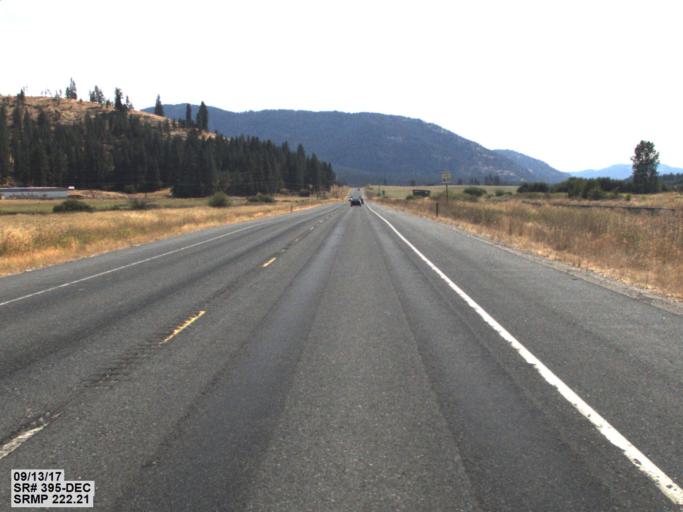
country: US
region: Washington
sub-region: Stevens County
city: Colville
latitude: 48.4453
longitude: -117.8704
